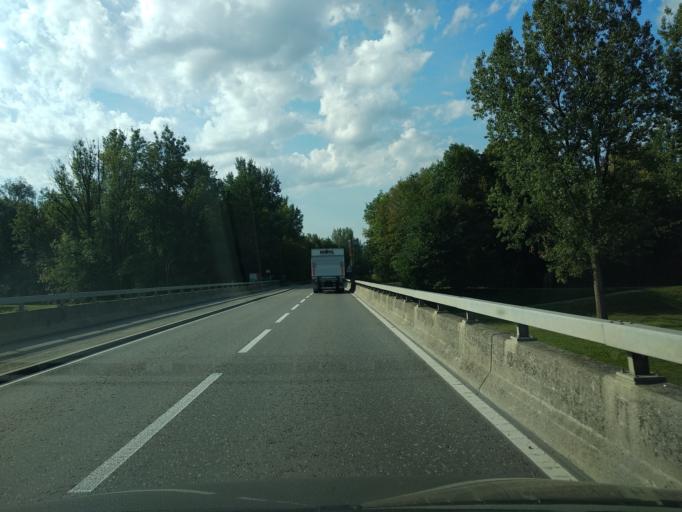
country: CH
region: Thurgau
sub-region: Frauenfeld District
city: Frauenfeld
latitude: 47.5794
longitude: 8.8844
